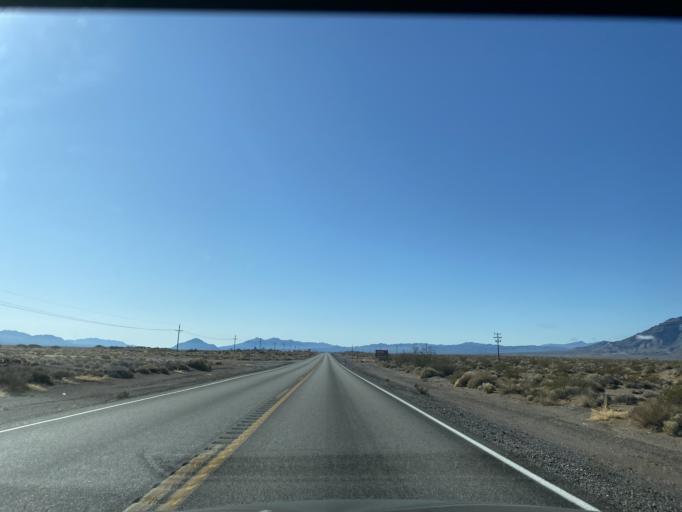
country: US
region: Nevada
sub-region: Nye County
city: Pahrump
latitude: 36.4359
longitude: -116.4221
